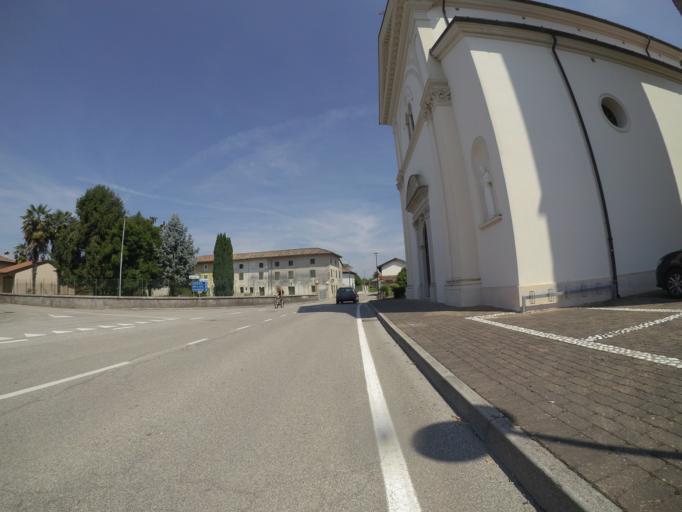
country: IT
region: Friuli Venezia Giulia
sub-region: Provincia di Udine
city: Varmo
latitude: 45.9003
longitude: 12.9633
